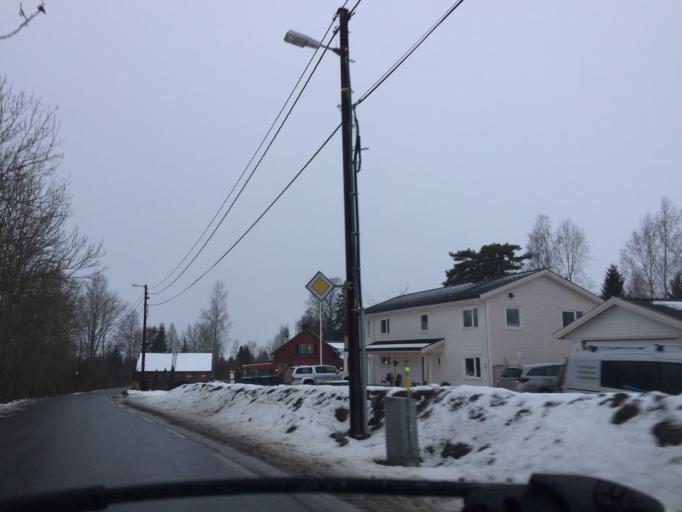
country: NO
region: Akershus
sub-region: As
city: As
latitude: 59.7023
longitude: 10.7565
